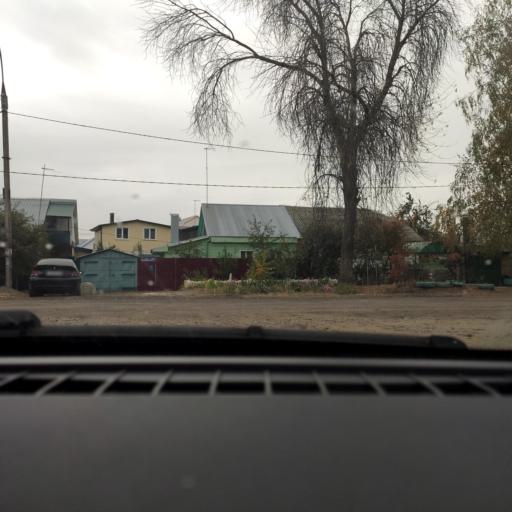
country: RU
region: Voronezj
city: Maslovka
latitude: 51.6315
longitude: 39.2759
